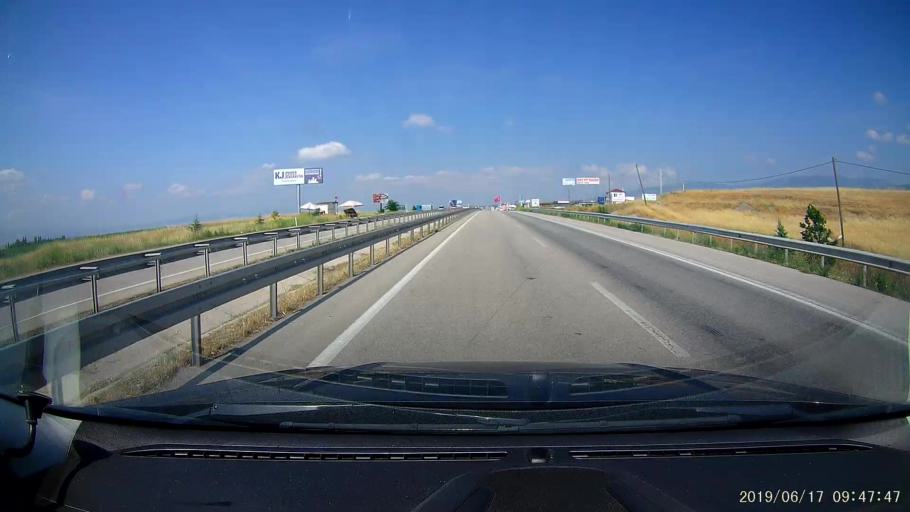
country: TR
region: Amasya
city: Suluova
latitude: 40.8759
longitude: 35.5701
